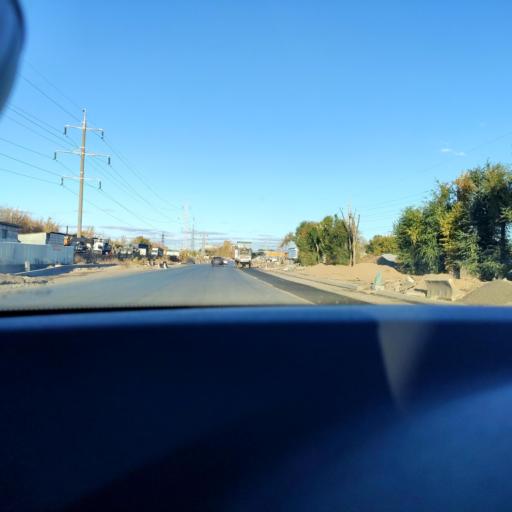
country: RU
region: Samara
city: Samara
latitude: 53.1918
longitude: 50.2283
